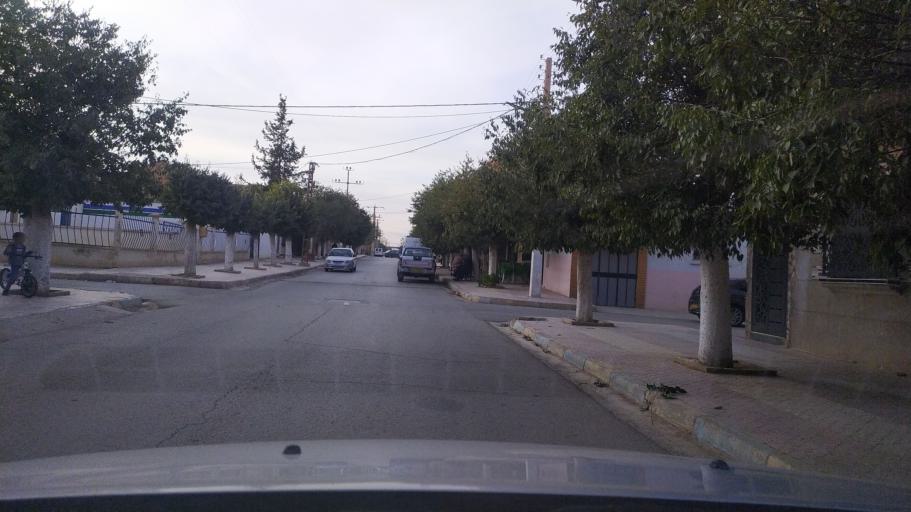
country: DZ
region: Tiaret
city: Frenda
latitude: 34.8988
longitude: 1.2390
